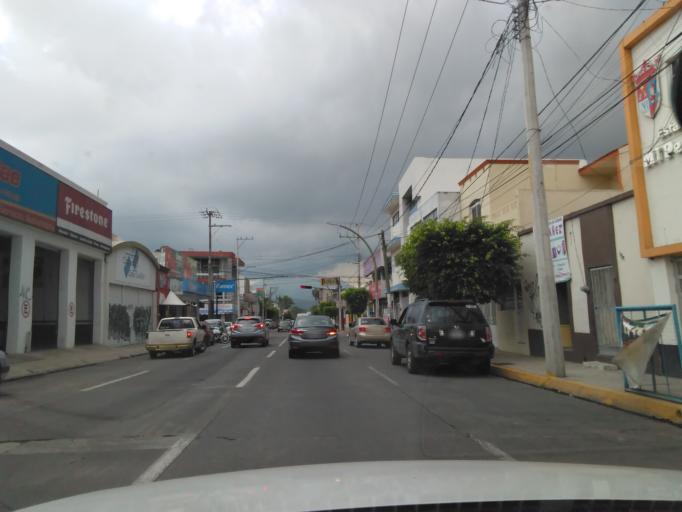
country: MX
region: Nayarit
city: Tepic
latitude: 21.5069
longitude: -104.8889
